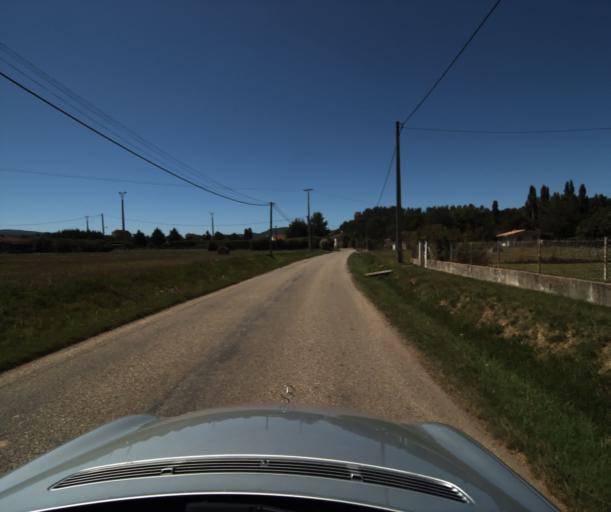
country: FR
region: Midi-Pyrenees
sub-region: Departement de l'Ariege
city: Belesta
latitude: 42.9882
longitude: 1.9172
